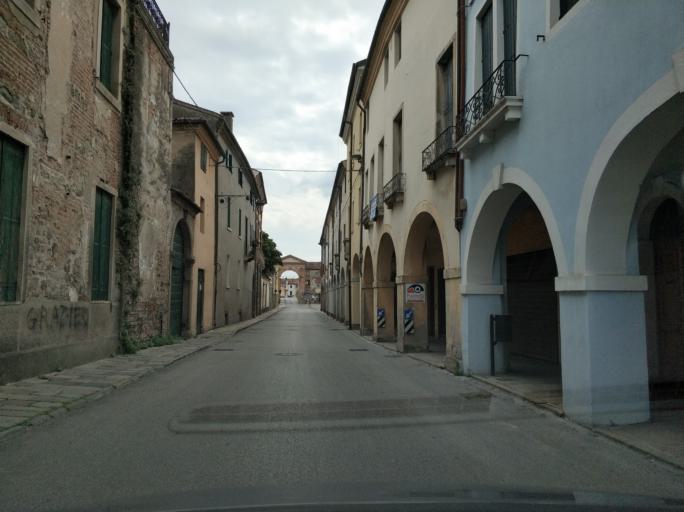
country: IT
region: Veneto
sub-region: Provincia di Padova
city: Este
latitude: 45.2293
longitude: 11.6533
